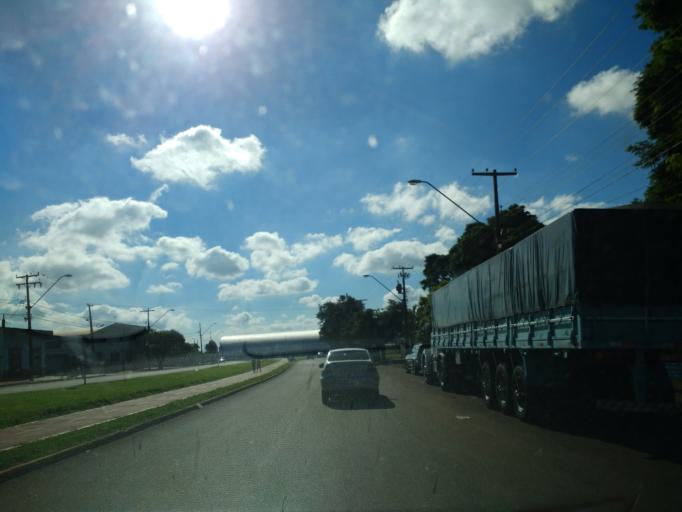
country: BR
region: Parana
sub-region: Palotina
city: Palotina
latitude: -24.3933
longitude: -53.5130
